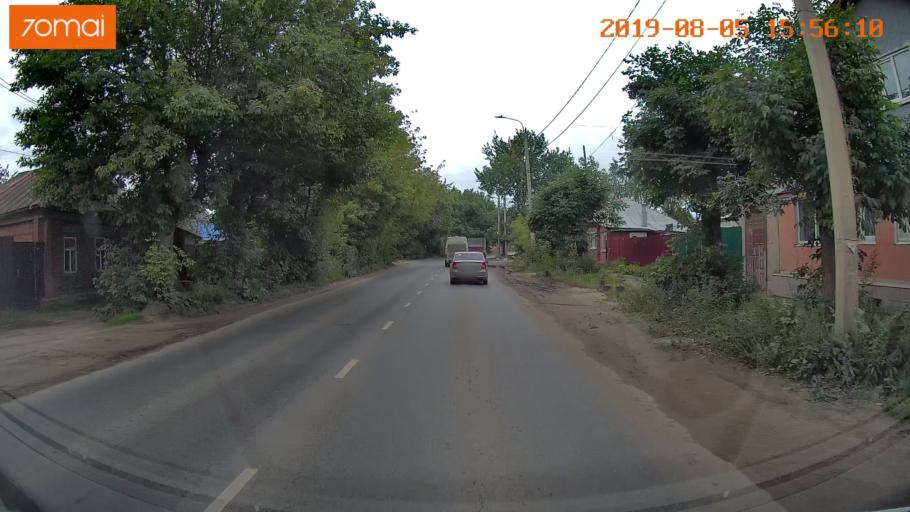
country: RU
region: Ivanovo
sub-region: Gorod Ivanovo
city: Ivanovo
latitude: 56.9936
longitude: 40.9525
